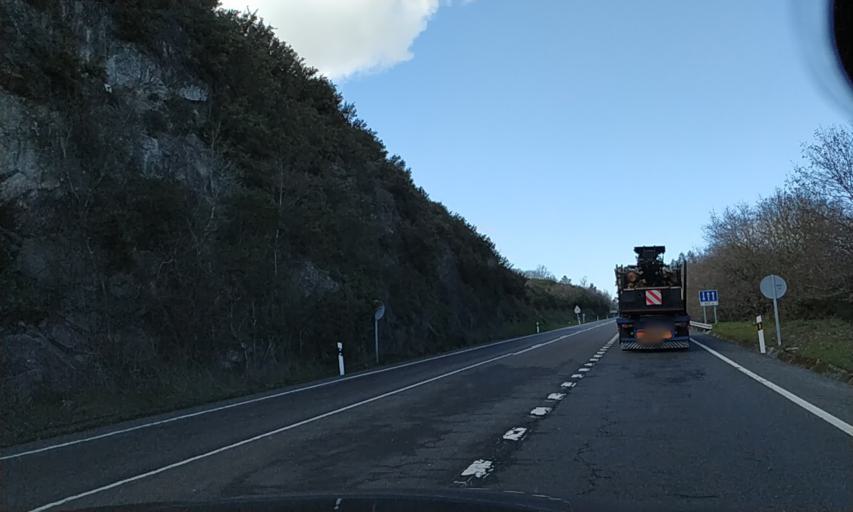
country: ES
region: Galicia
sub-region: Provincia de Pontevedra
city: Silleda
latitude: 42.7009
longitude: -8.3398
